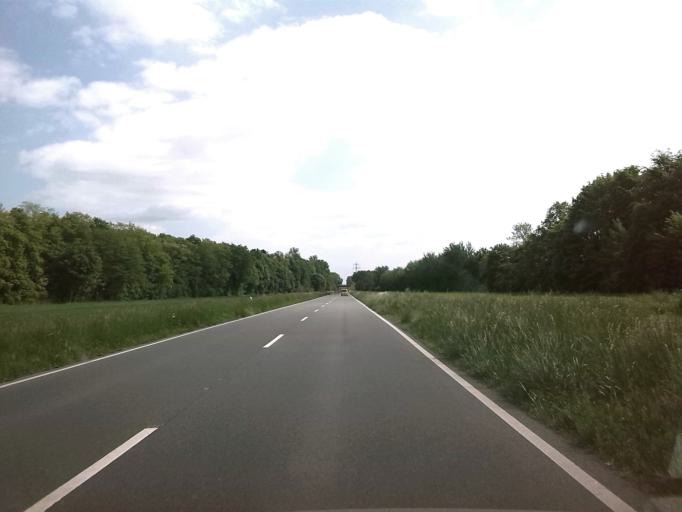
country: DE
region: Hesse
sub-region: Regierungsbezirk Darmstadt
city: Gross-Zimmern
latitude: 49.8800
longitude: 8.8060
